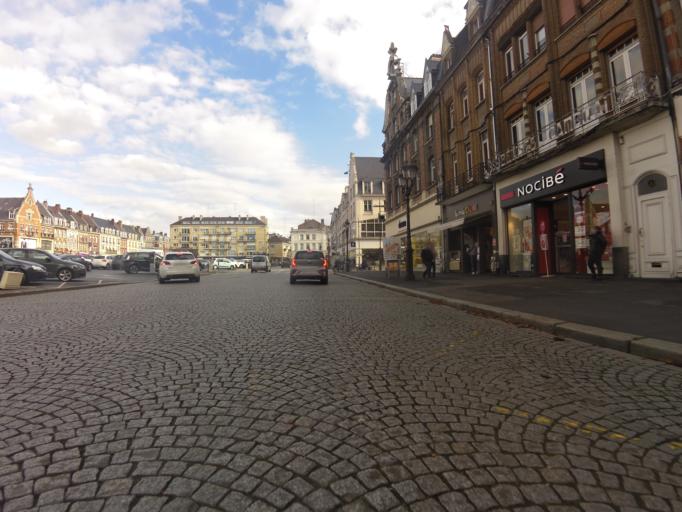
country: FR
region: Nord-Pas-de-Calais
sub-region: Departement du Nord
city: Cambrai
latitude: 50.1755
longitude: 3.2337
